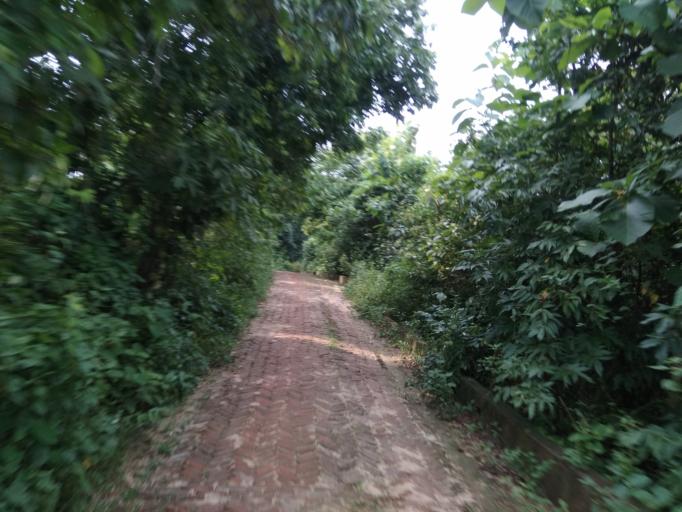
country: BD
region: Chittagong
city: Manikchari
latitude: 22.9251
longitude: 91.9121
